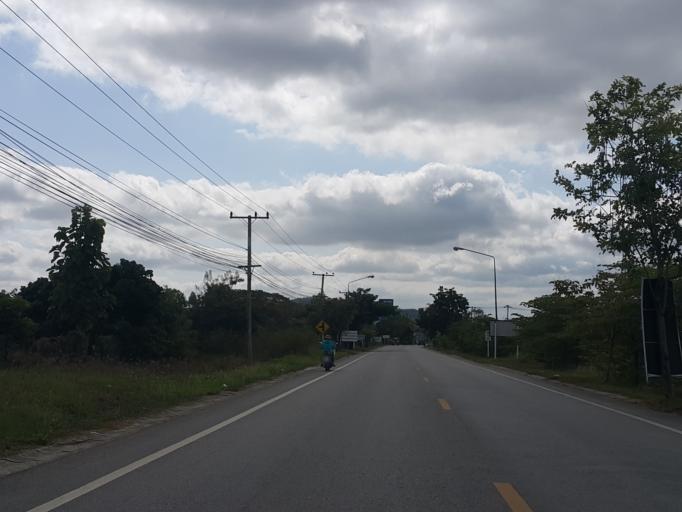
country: TH
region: Lamphun
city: Ban Thi
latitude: 18.6372
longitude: 99.1050
